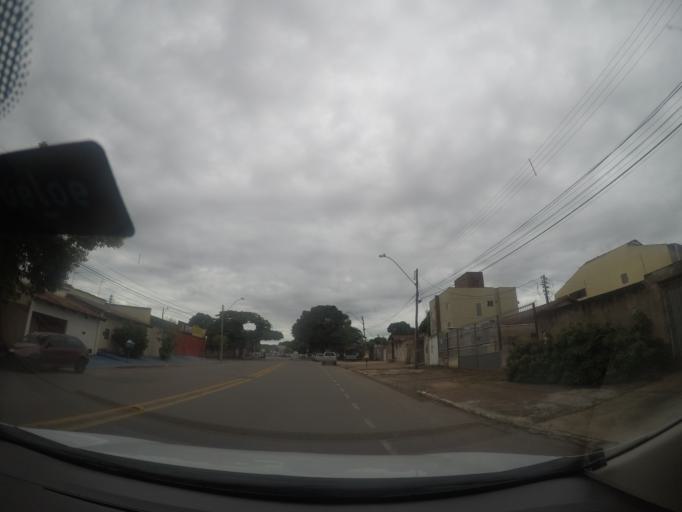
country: BR
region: Goias
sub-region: Goiania
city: Goiania
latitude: -16.6125
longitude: -49.2954
